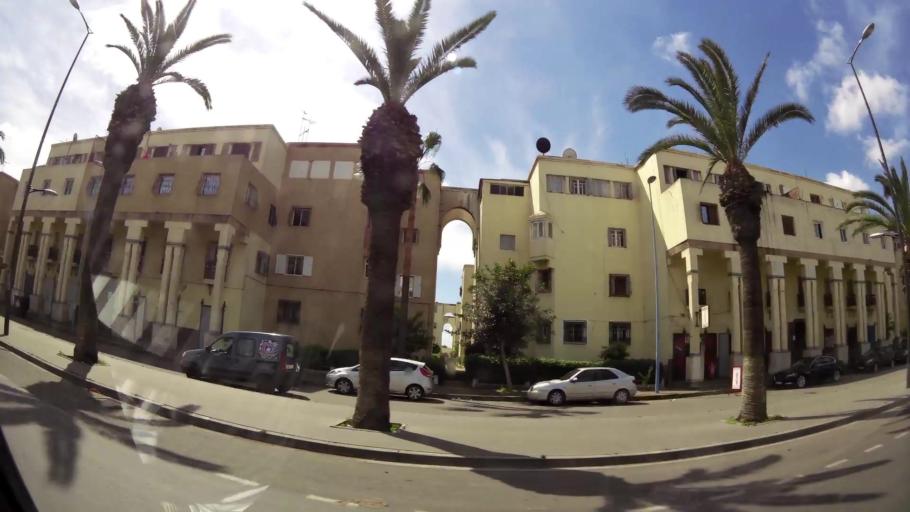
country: MA
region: Grand Casablanca
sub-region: Casablanca
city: Casablanca
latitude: 33.5997
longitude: -7.5655
